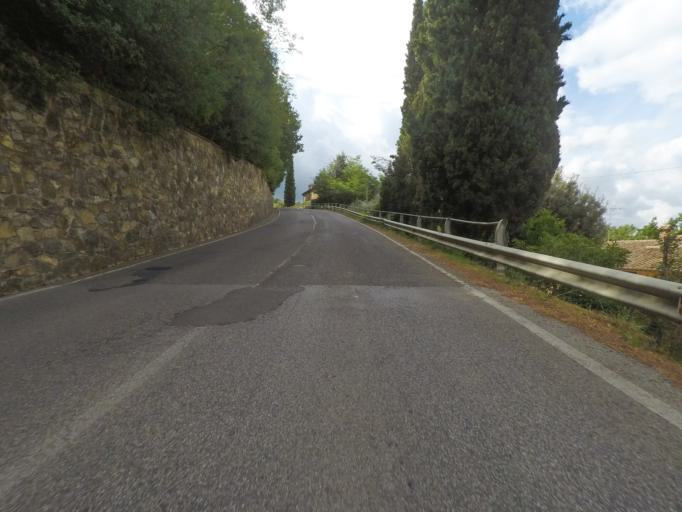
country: IT
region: Tuscany
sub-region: Provincia di Siena
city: Montepulciano
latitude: 43.1127
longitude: 11.7889
